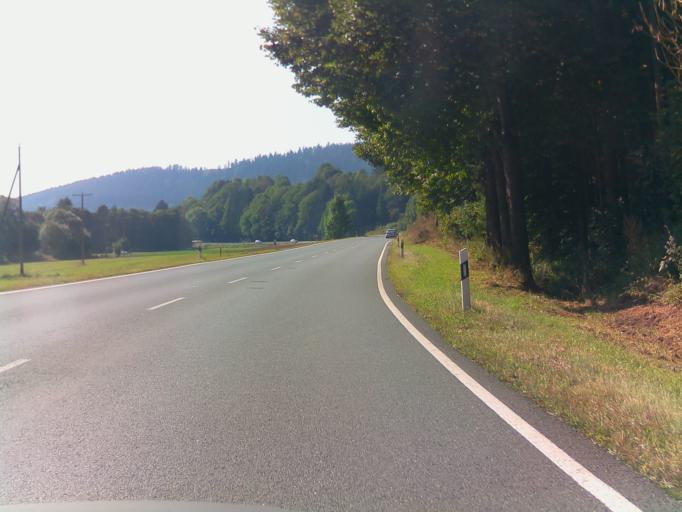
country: DE
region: Bavaria
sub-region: Upper Franconia
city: Pressig
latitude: 50.3696
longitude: 11.3273
